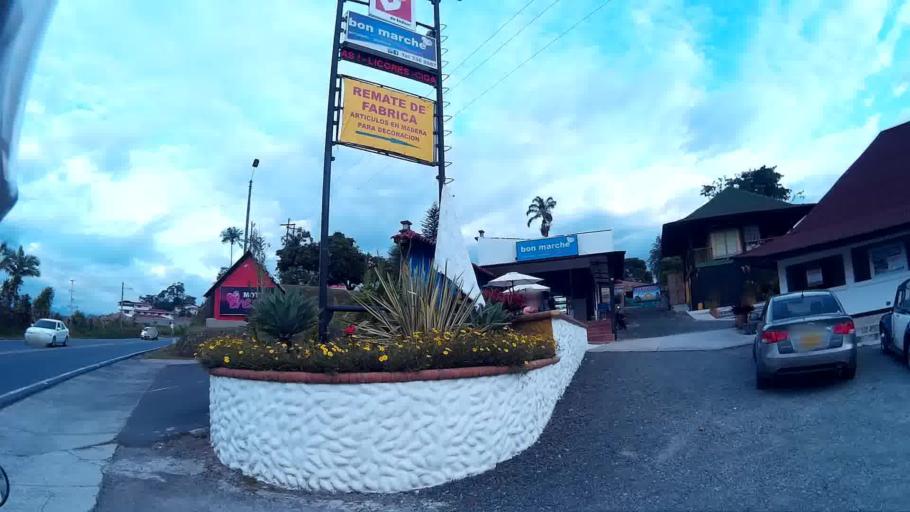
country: CO
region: Risaralda
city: Pereira
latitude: 4.7644
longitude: -75.6870
